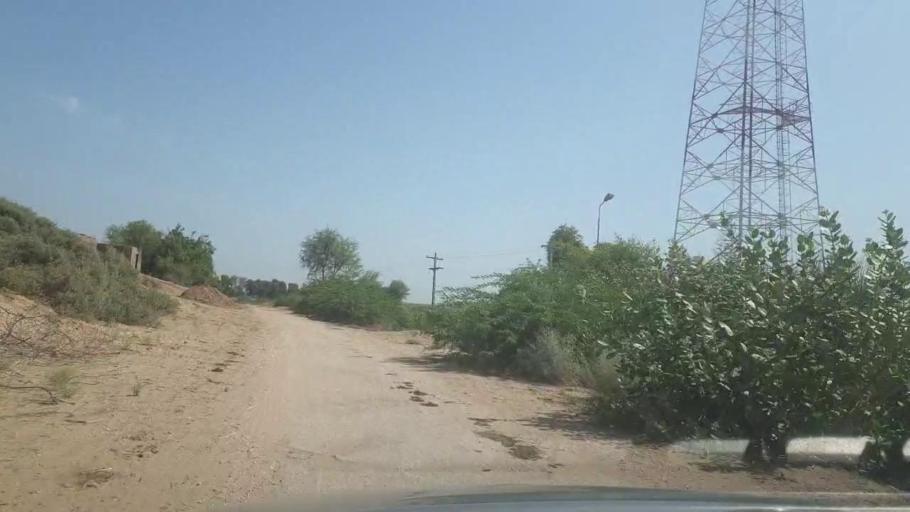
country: PK
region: Sindh
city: Khairpur
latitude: 27.4017
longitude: 69.0807
